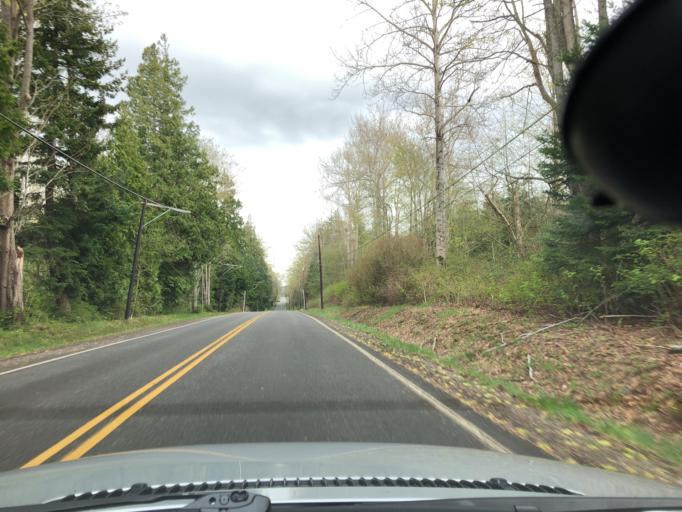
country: US
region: Washington
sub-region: Whatcom County
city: Birch Bay
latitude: 48.8926
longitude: -122.7784
